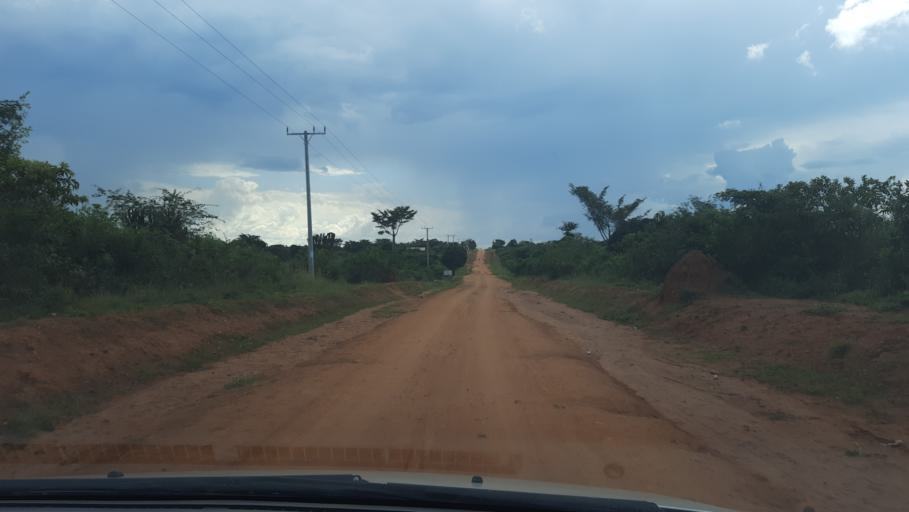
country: UG
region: Central Region
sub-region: Nakasongola District
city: Nakasongola
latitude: 1.3804
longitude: 32.5063
